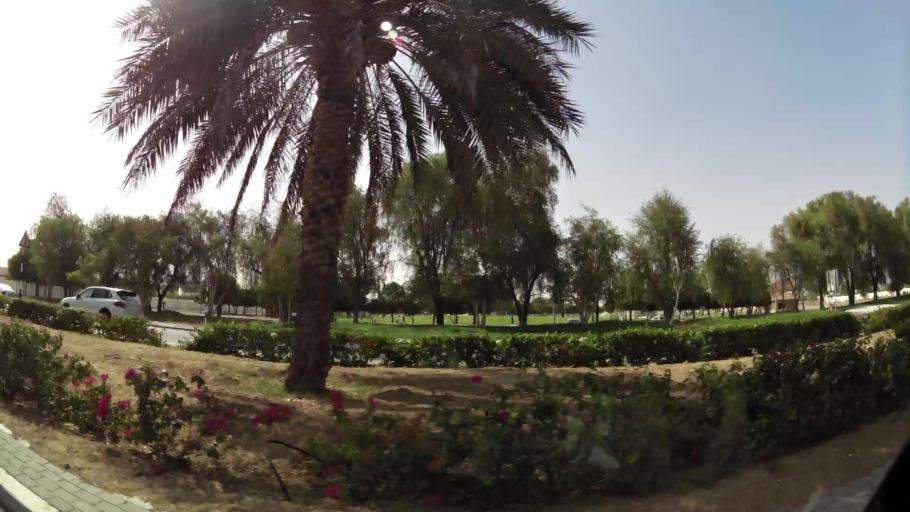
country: AE
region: Abu Dhabi
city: Al Ain
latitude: 24.2417
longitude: 55.7007
